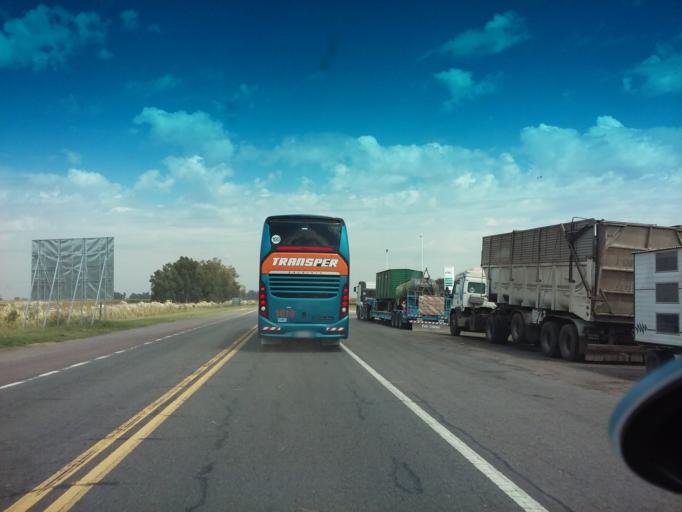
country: AR
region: Buenos Aires
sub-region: Partido de Carlos Casares
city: Carlos Casares
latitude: -35.6571
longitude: -61.3990
